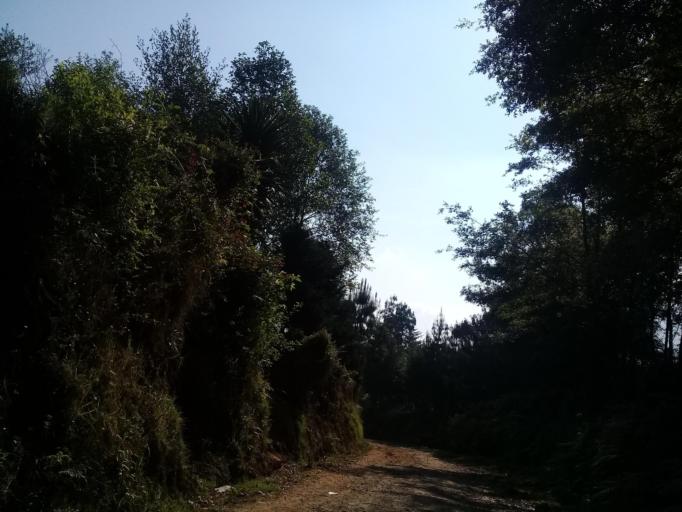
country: MX
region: Veracruz
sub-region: Mariano Escobedo
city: San Isidro el Berro
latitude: 18.9446
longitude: -97.2155
